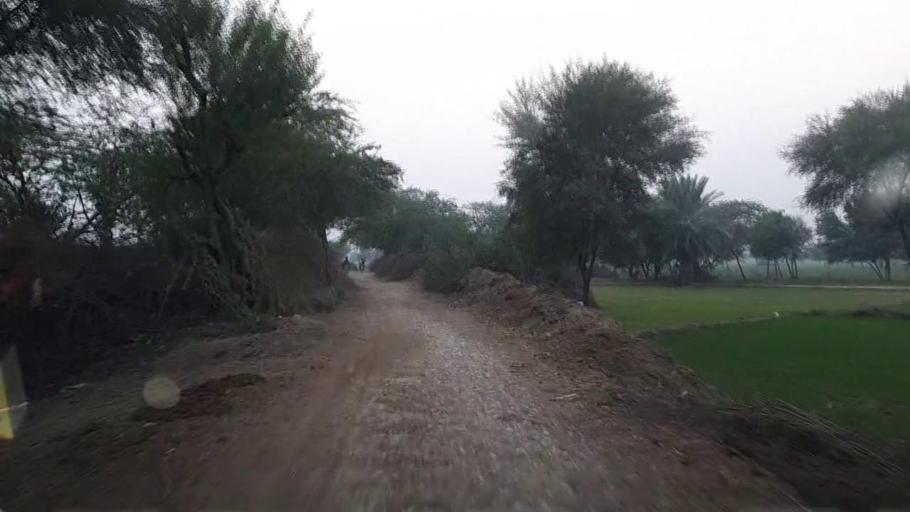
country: PK
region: Sindh
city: Kandiari
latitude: 26.9621
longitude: 68.4640
